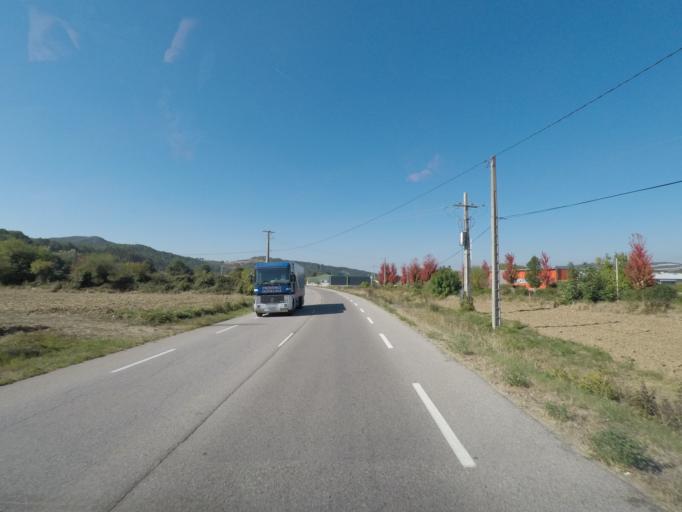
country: FR
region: Rhone-Alpes
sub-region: Departement de la Drome
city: Aouste-sur-Sye
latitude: 44.7095
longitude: 5.0666
